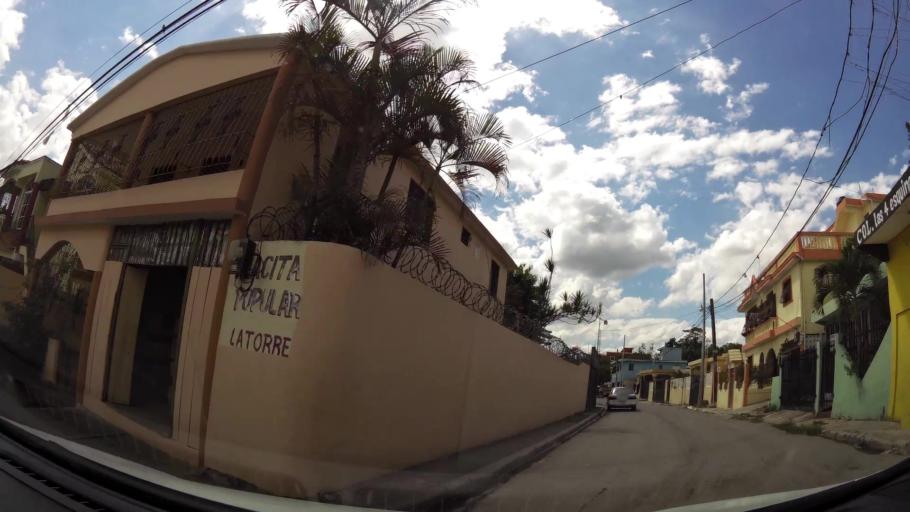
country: DO
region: Nacional
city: Ensanche Luperon
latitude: 18.5338
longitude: -69.9082
